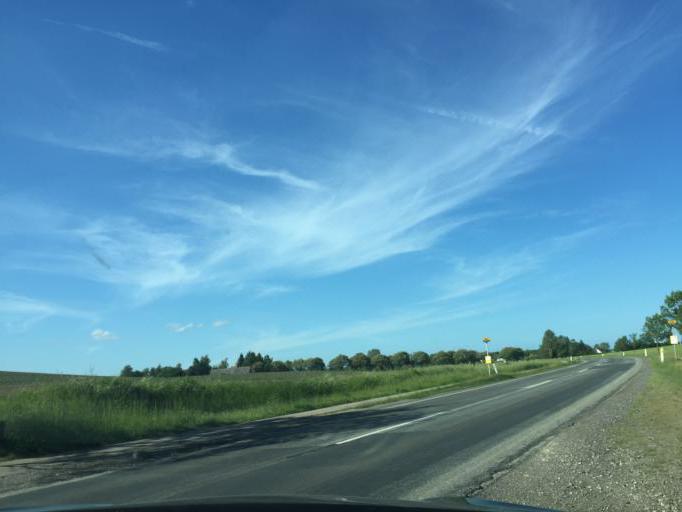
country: DK
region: Zealand
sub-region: Stevns Kommune
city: Harlev
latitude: 55.3648
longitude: 12.2540
